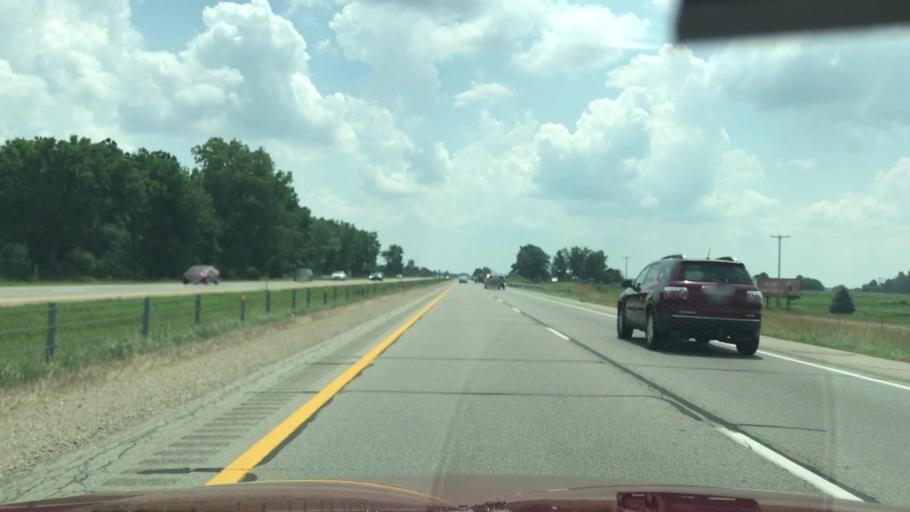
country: US
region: Michigan
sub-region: Allegan County
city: Wayland
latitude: 42.6473
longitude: -85.6622
